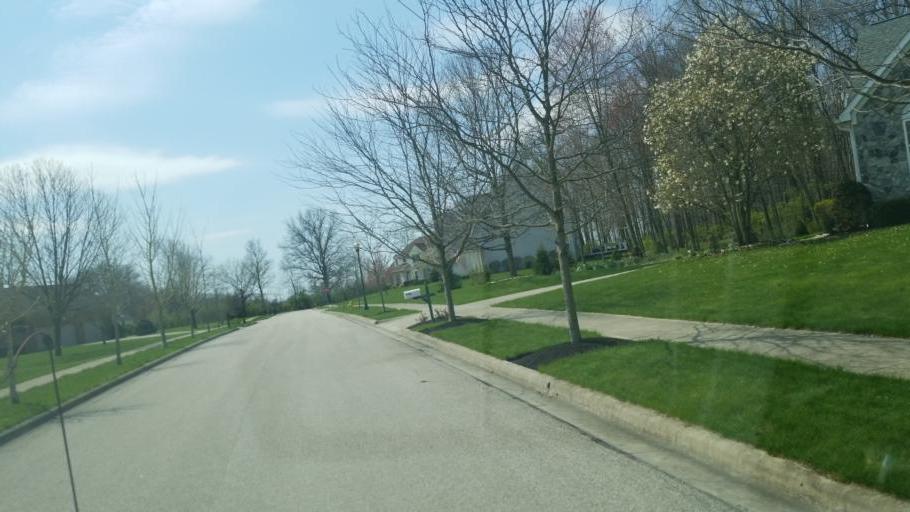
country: US
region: Ohio
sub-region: Delaware County
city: Delaware
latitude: 40.3297
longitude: -83.0871
